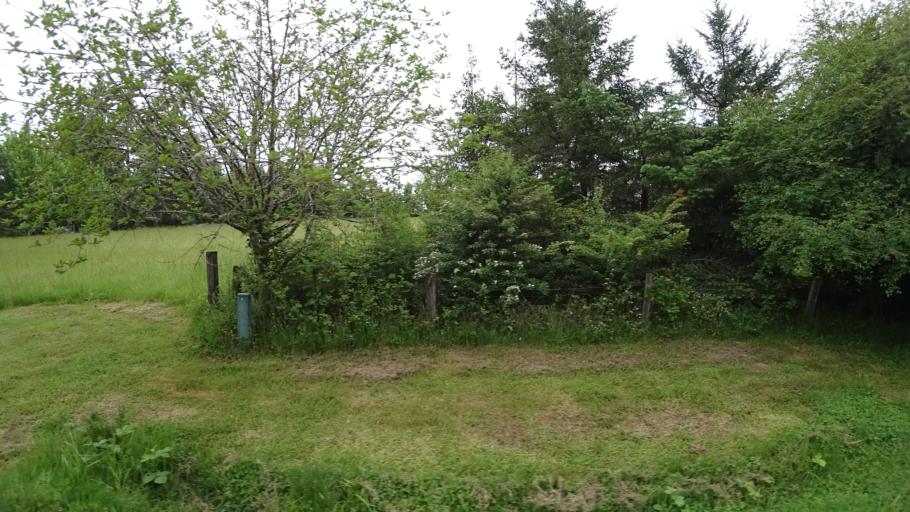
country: US
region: Oregon
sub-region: Washington County
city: Aloha
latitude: 45.4842
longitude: -122.9116
